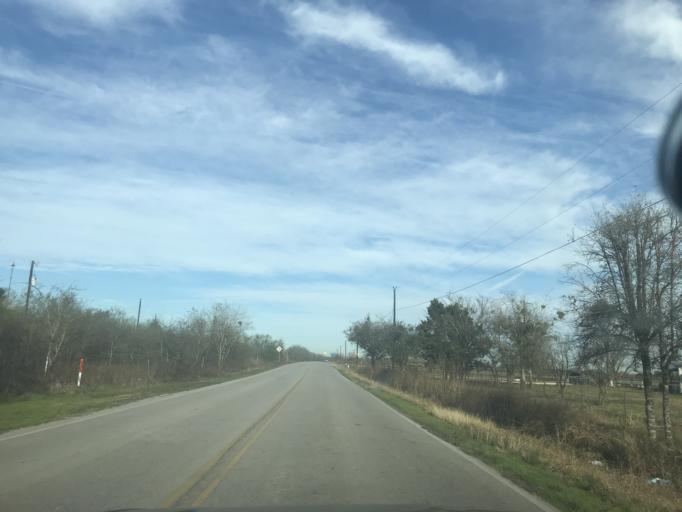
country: US
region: Texas
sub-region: Travis County
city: Manor
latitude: 30.2935
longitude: -97.5236
